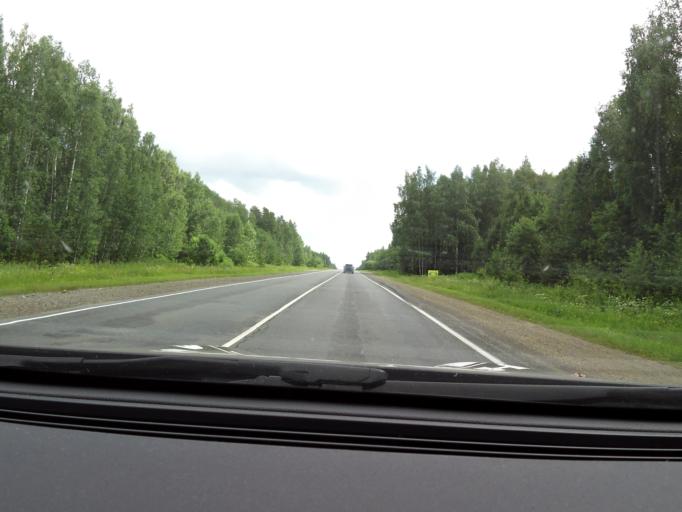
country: RU
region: Sverdlovsk
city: Achit
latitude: 56.8726
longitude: 57.6545
